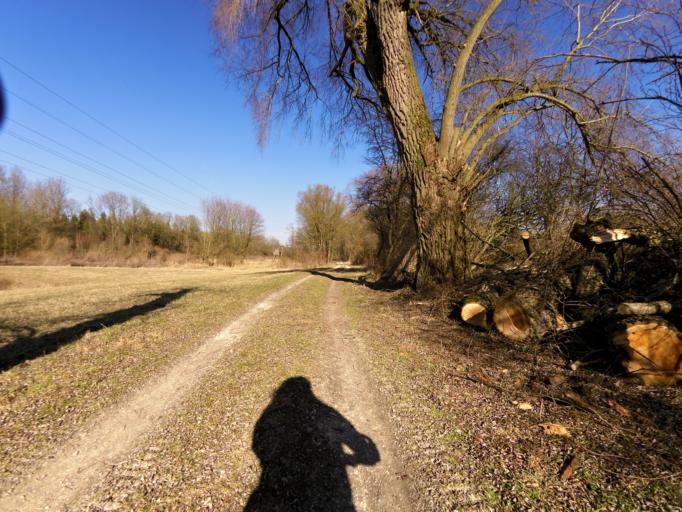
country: DE
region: Bavaria
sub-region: Lower Bavaria
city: Eching
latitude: 48.5054
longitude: 12.0337
